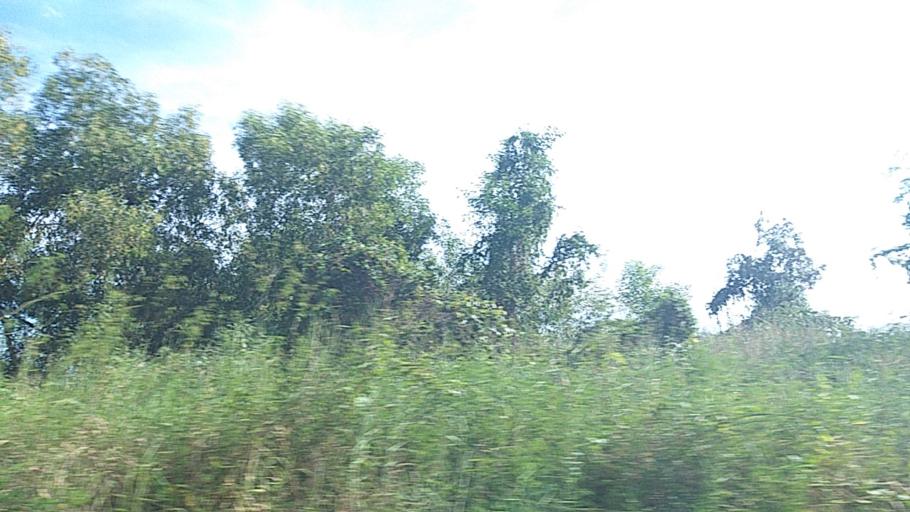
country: TH
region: Pathum Thani
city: Thanyaburi
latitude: 14.0201
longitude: 100.7384
